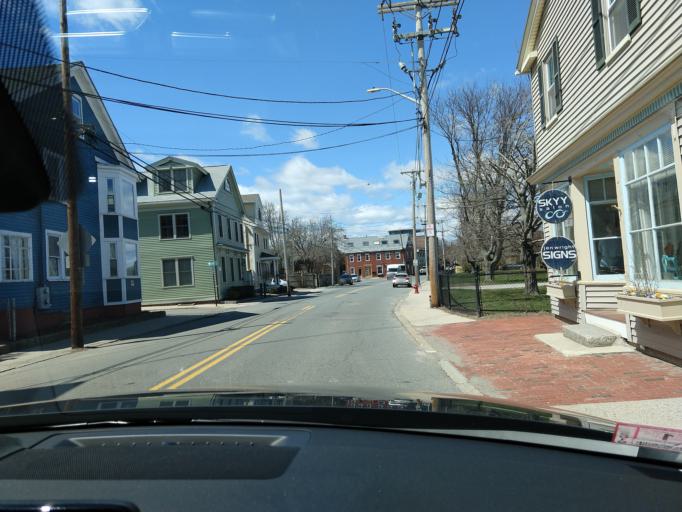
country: US
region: Massachusetts
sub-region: Essex County
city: Newburyport
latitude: 42.8098
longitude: -70.8640
